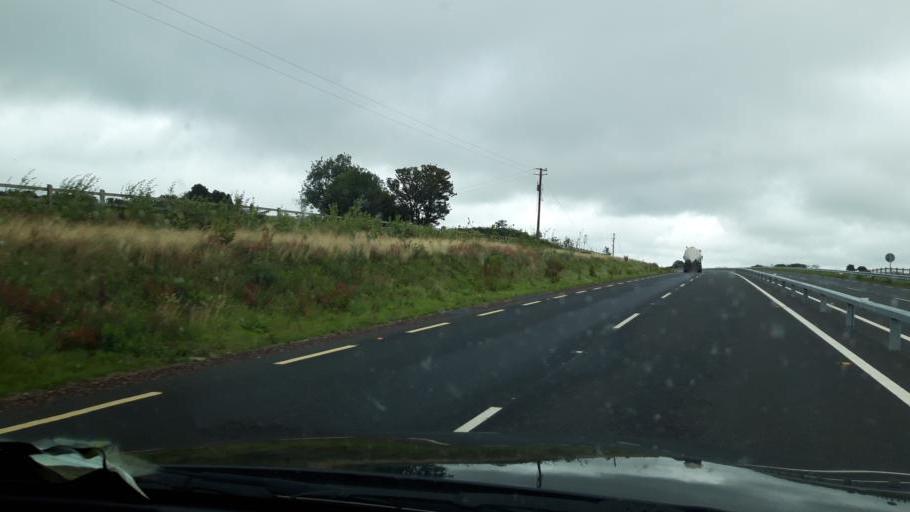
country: IE
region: Leinster
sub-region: Loch Garman
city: New Ross
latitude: 52.3912
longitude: -6.8815
